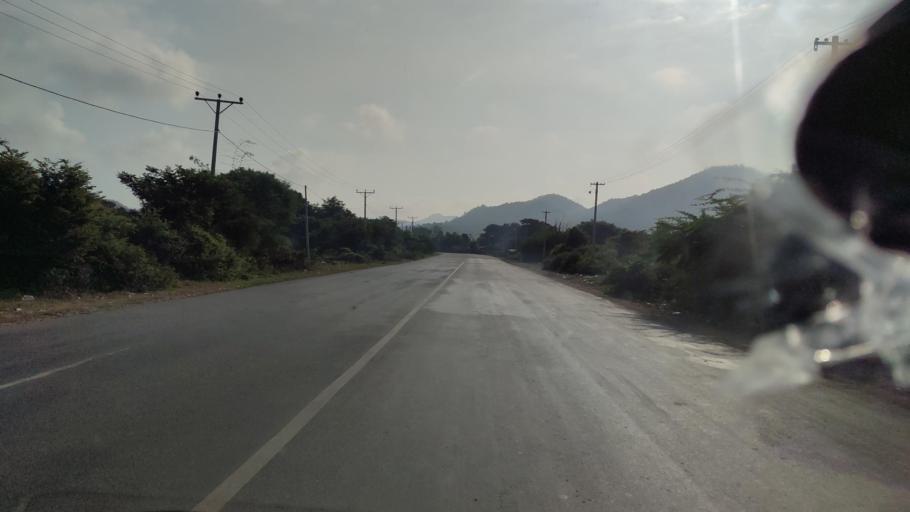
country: MM
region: Mandalay
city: Yamethin
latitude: 20.7518
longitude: 96.2642
